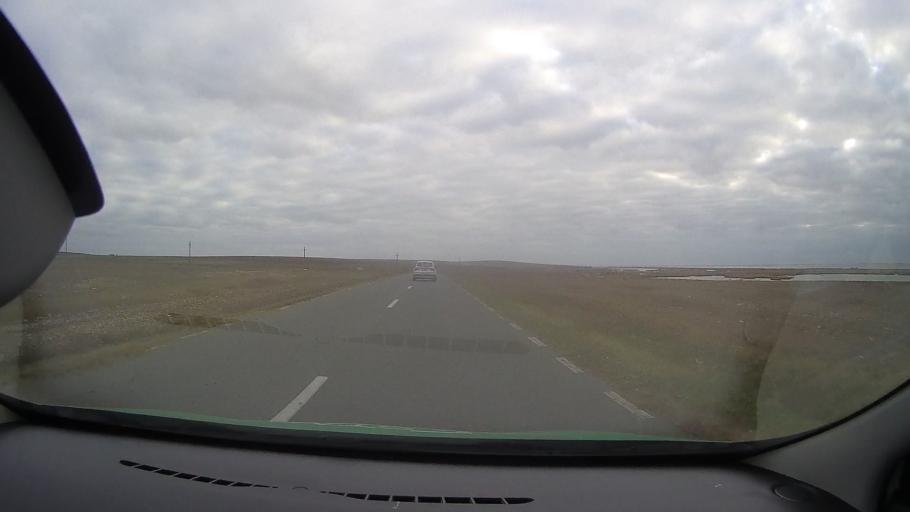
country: RO
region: Tulcea
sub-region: Comuna Jurilovca
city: Jurilovca
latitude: 44.7606
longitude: 28.8872
